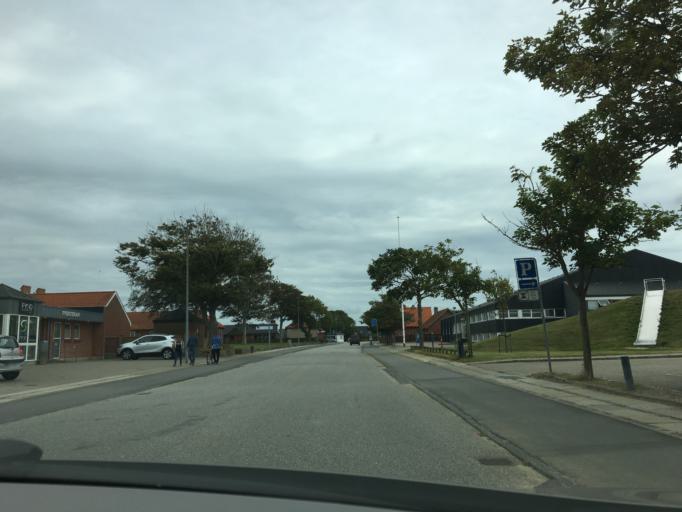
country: DK
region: Central Jutland
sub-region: Ringkobing-Skjern Kommune
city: Ringkobing
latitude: 56.0856
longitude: 8.2518
